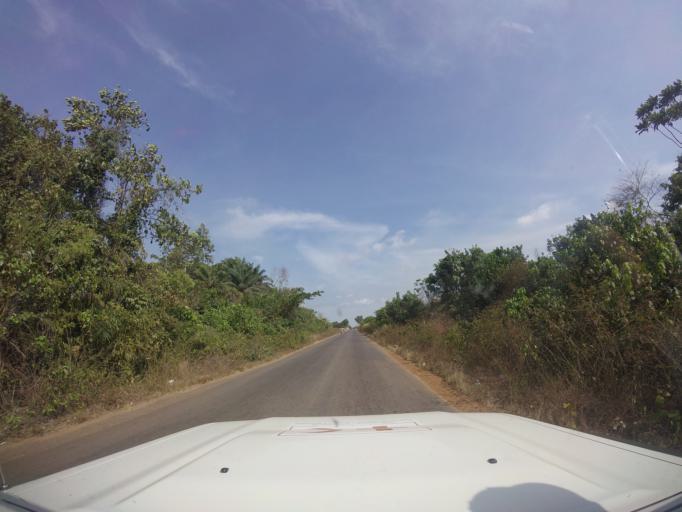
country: LR
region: Bomi
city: Tubmanburg
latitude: 6.7261
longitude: -10.9858
